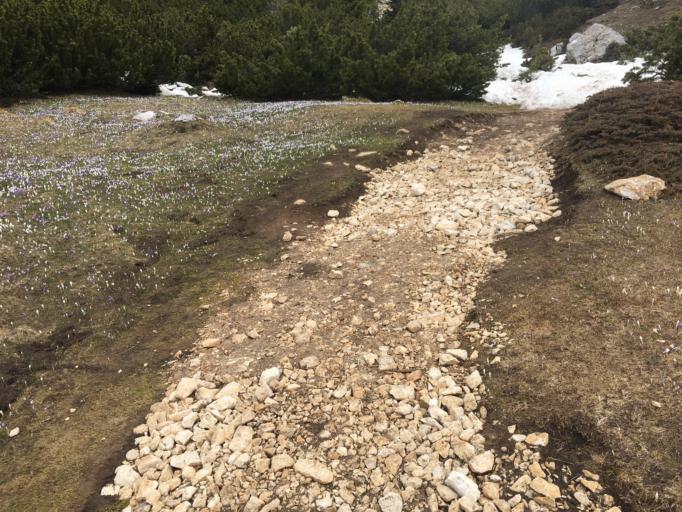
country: IT
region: Trentino-Alto Adige
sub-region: Provincia di Trento
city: Varena
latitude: 46.3504
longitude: 11.4451
